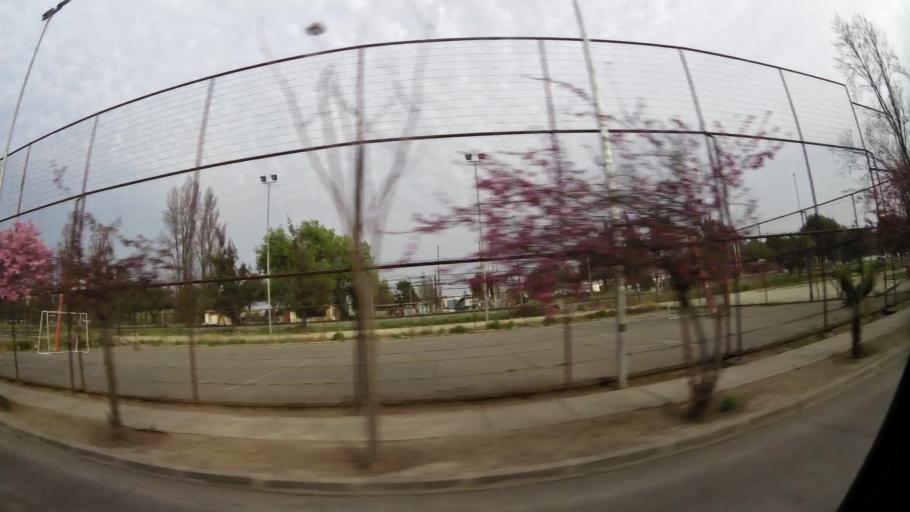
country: CL
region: Santiago Metropolitan
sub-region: Provincia de Maipo
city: San Bernardo
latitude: -33.5343
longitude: -70.7684
